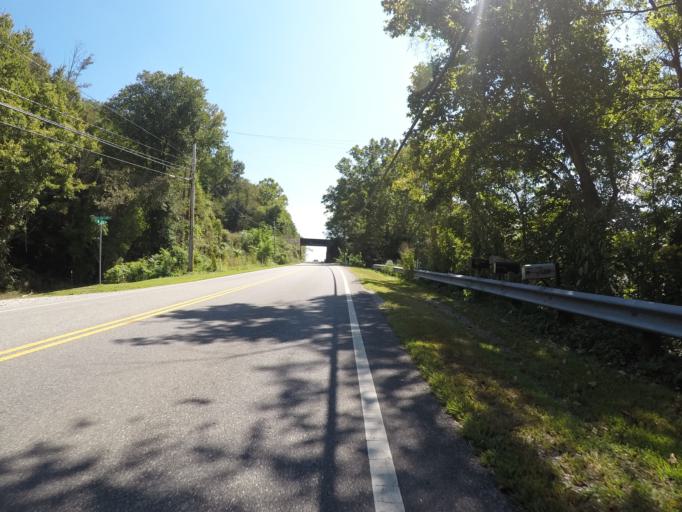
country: US
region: West Virginia
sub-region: Wayne County
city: Kenova
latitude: 38.4088
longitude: -82.5729
